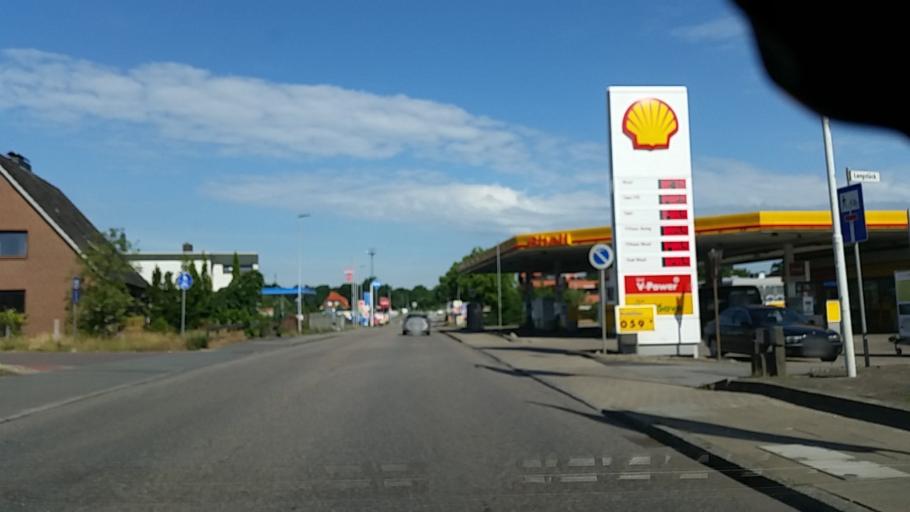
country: DE
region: Schleswig-Holstein
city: Kaltenkirchen
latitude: 53.8403
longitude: 9.9492
